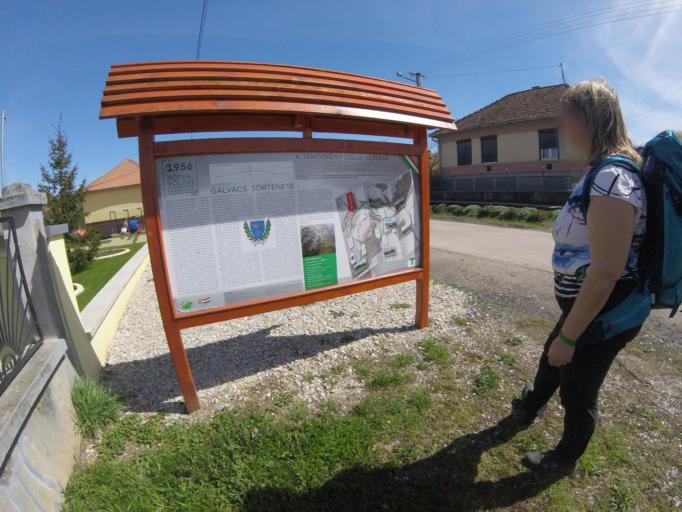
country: HU
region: Borsod-Abauj-Zemplen
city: Szendro
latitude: 48.4195
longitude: 20.7779
